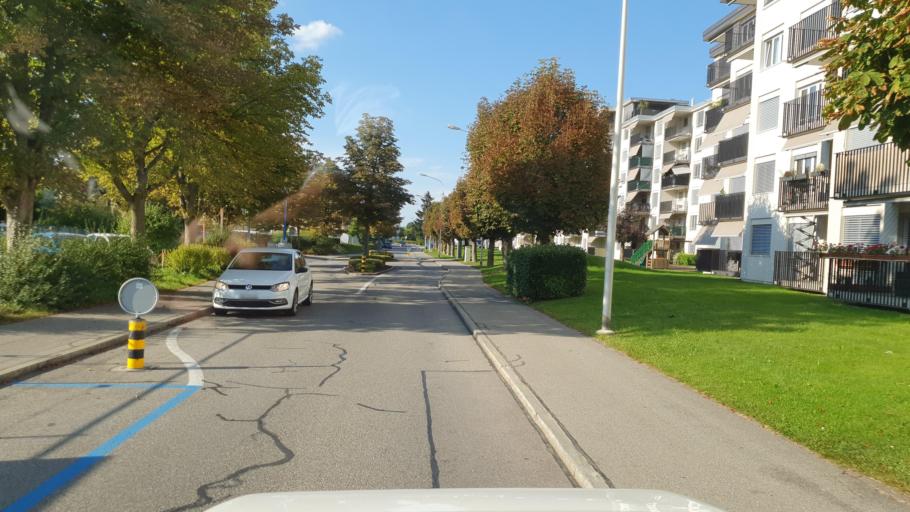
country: CH
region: Aargau
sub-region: Bezirk Muri
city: Muri
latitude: 47.2736
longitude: 8.3458
